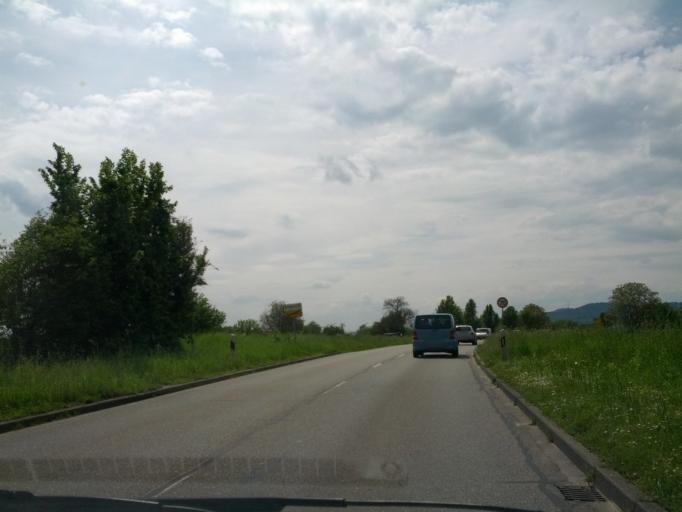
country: DE
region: Baden-Wuerttemberg
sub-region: Freiburg Region
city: Teningen
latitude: 48.1246
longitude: 7.8078
